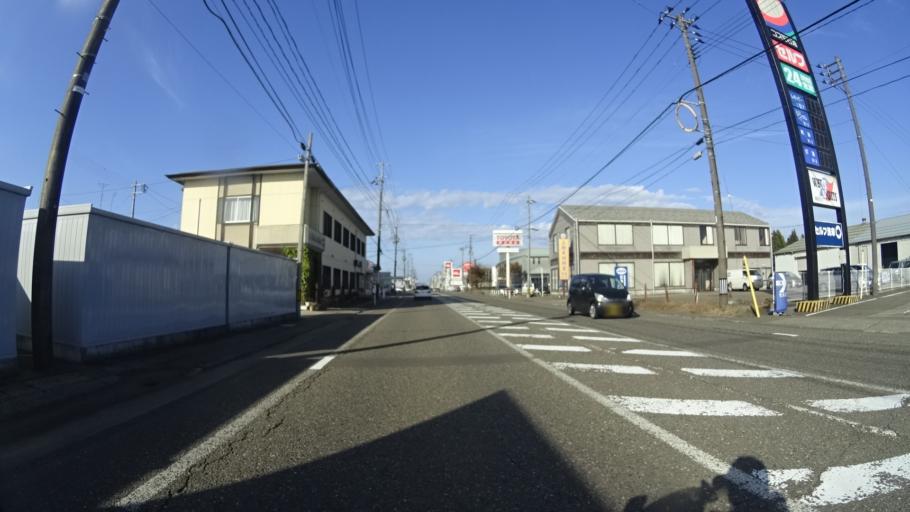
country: JP
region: Niigata
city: Joetsu
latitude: 37.1552
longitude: 138.2382
